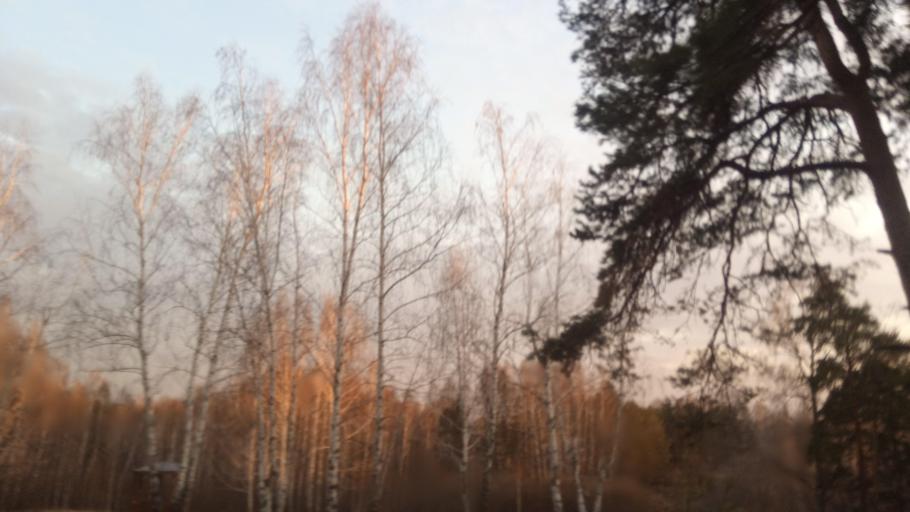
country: RU
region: Chelyabinsk
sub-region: Gorod Chelyabinsk
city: Chelyabinsk
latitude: 55.1592
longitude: 61.3237
